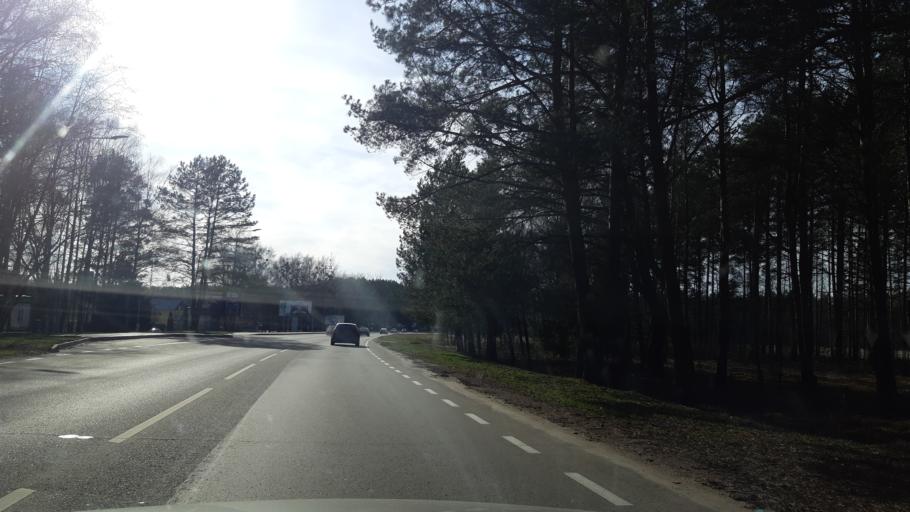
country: LT
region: Alytaus apskritis
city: Druskininkai
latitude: 54.0051
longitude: 24.0184
